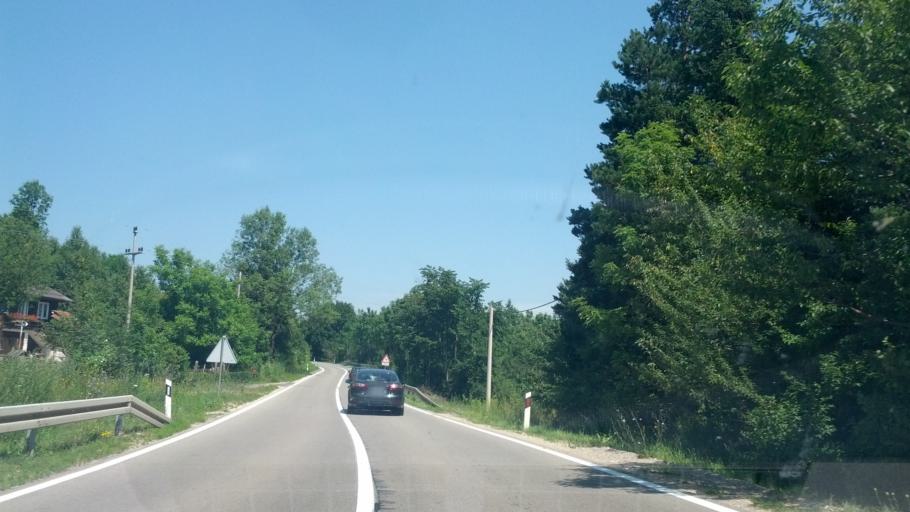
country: BA
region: Federation of Bosnia and Herzegovina
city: Izacic
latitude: 44.8849
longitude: 15.7275
